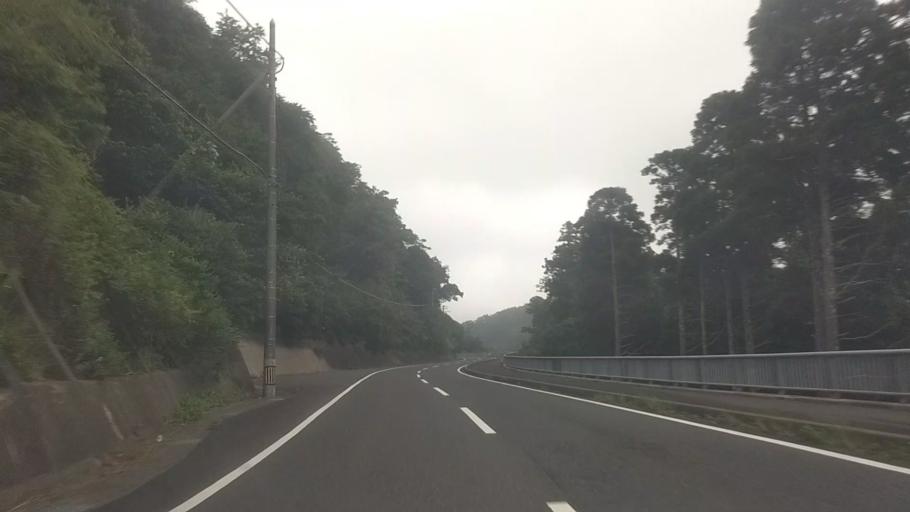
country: JP
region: Chiba
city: Kawaguchi
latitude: 35.1433
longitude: 140.1507
